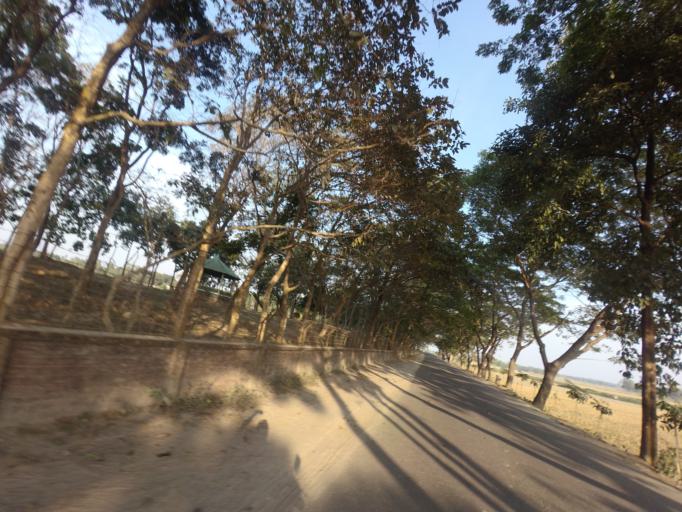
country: BD
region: Rajshahi
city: Saidpur
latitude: 26.0011
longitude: 88.7557
